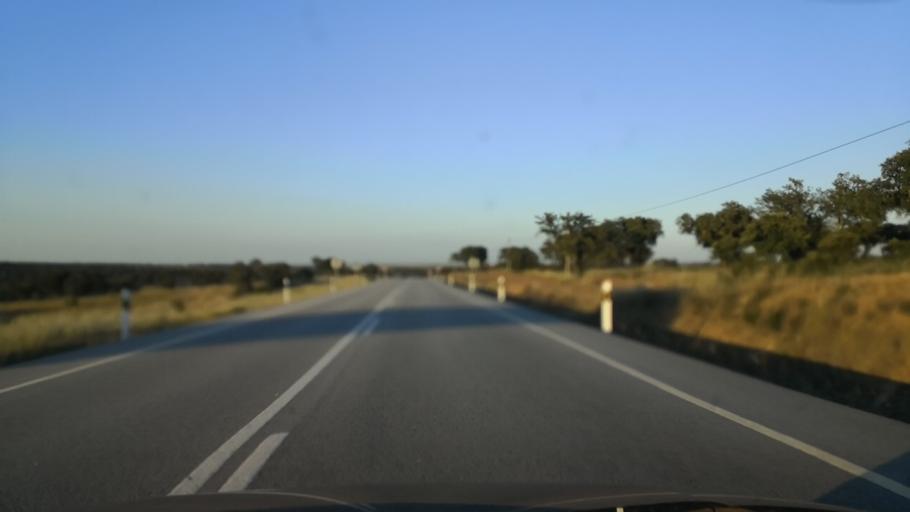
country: ES
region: Extremadura
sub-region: Provincia de Caceres
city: Salorino
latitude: 39.5109
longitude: -7.0946
